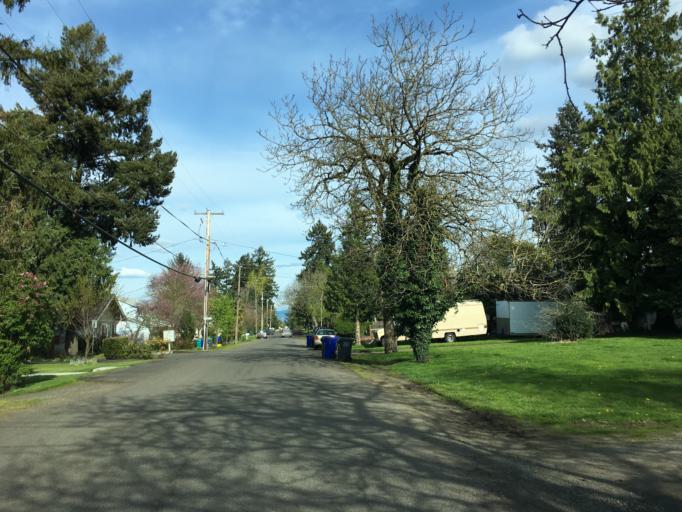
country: US
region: Oregon
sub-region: Multnomah County
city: Lents
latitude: 45.5499
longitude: -122.5533
